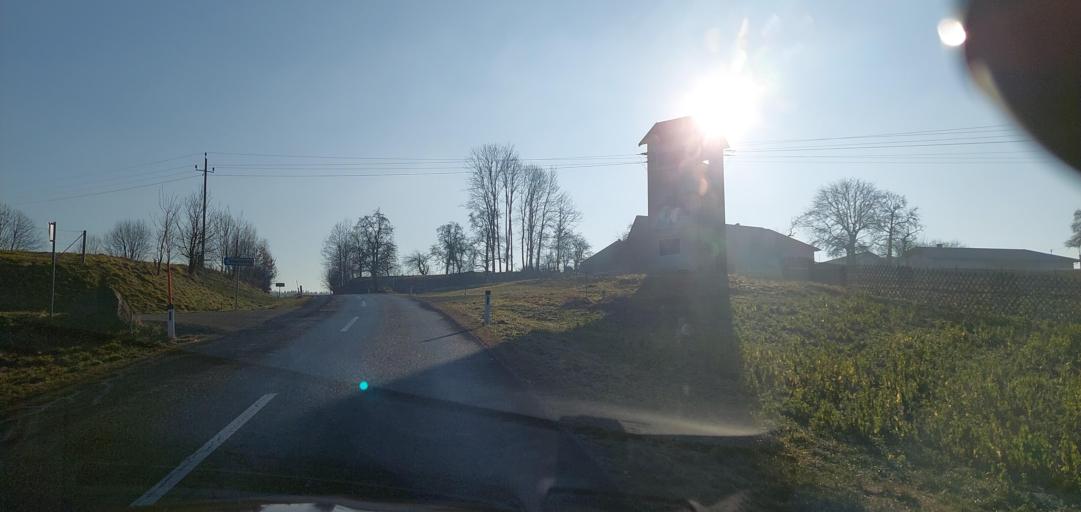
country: AT
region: Upper Austria
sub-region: Politischer Bezirk Grieskirchen
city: Grieskirchen
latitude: 48.1945
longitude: 13.8404
